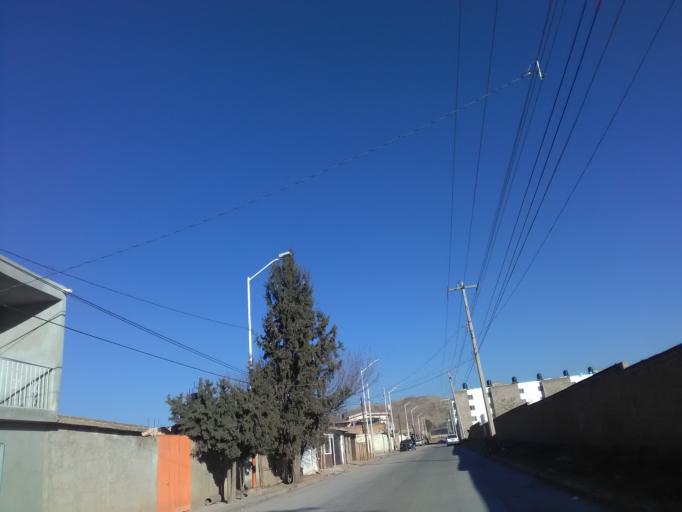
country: MX
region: Durango
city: Victoria de Durango
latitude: 24.0537
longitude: -104.6528
